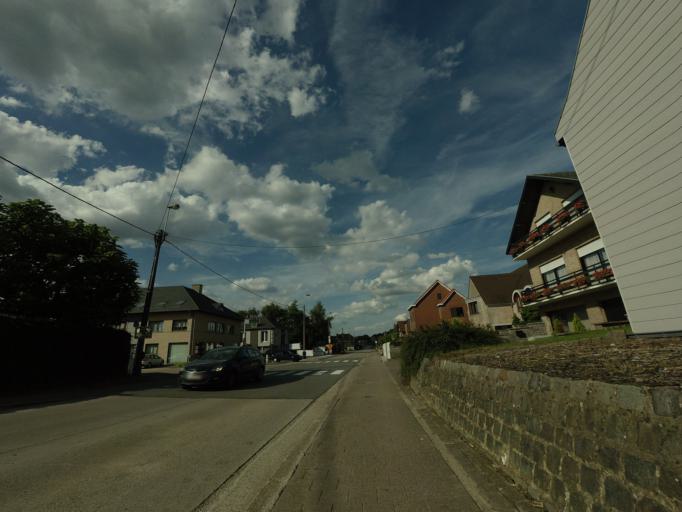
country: BE
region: Flanders
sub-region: Provincie Vlaams-Brabant
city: Meise
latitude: 50.9581
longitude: 4.3430
